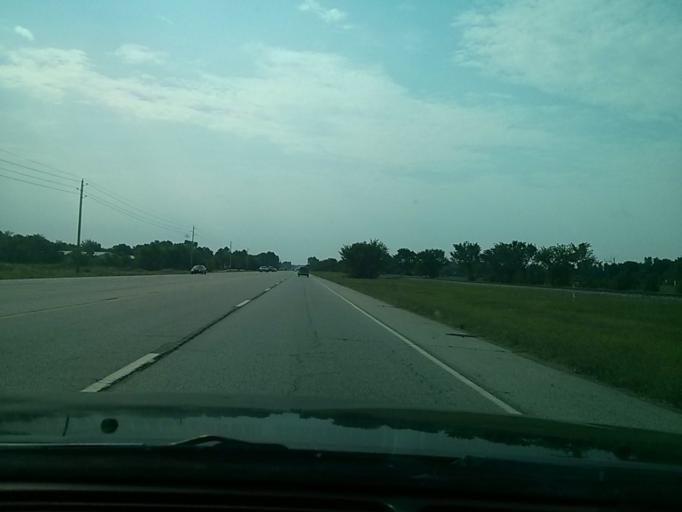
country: US
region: Oklahoma
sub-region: Wagoner County
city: Coweta
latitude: 35.9978
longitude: -95.6777
